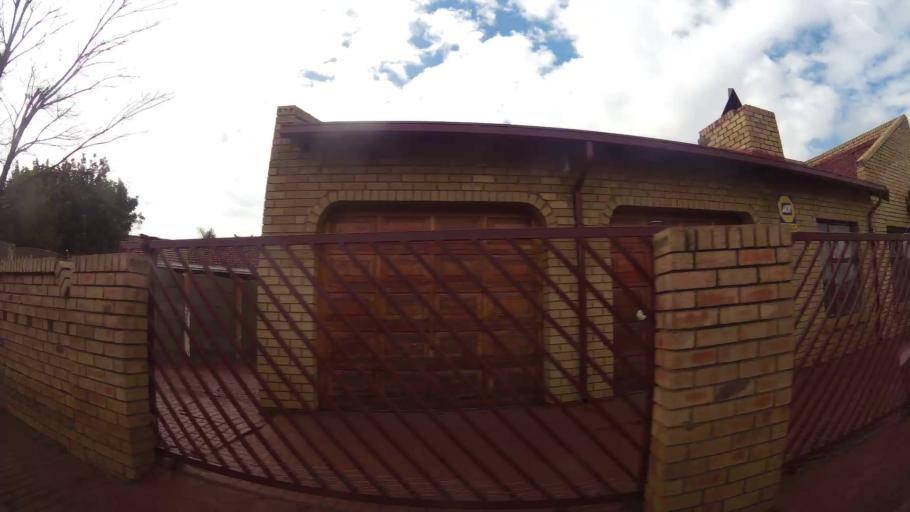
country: ZA
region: Gauteng
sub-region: Ekurhuleni Metropolitan Municipality
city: Germiston
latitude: -26.3259
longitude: 28.1811
